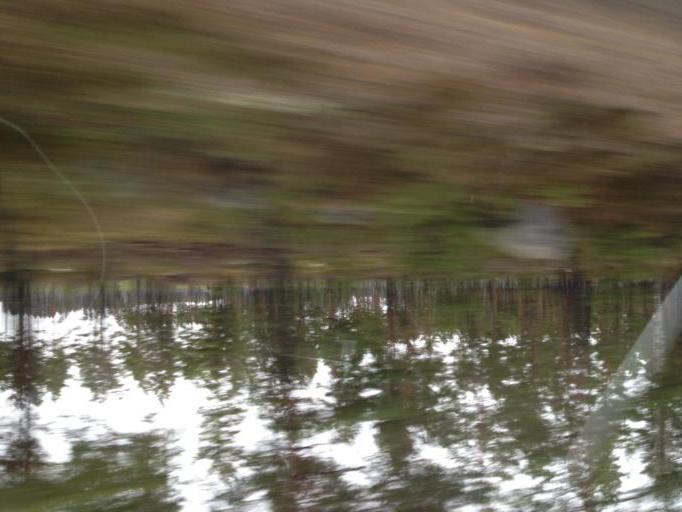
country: FI
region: Uusimaa
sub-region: Raaseporin
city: Hanko
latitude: 59.8483
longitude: 23.0052
